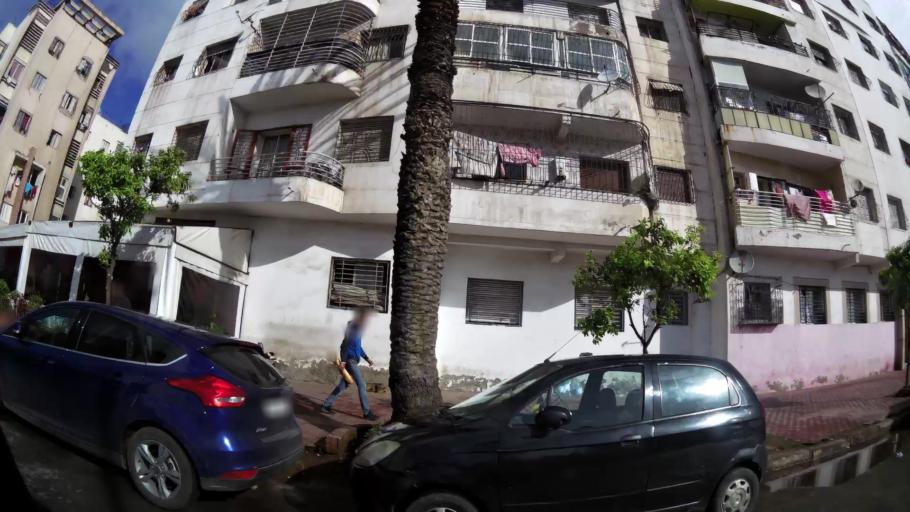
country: MA
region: Grand Casablanca
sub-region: Casablanca
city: Casablanca
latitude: 33.5657
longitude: -7.5787
